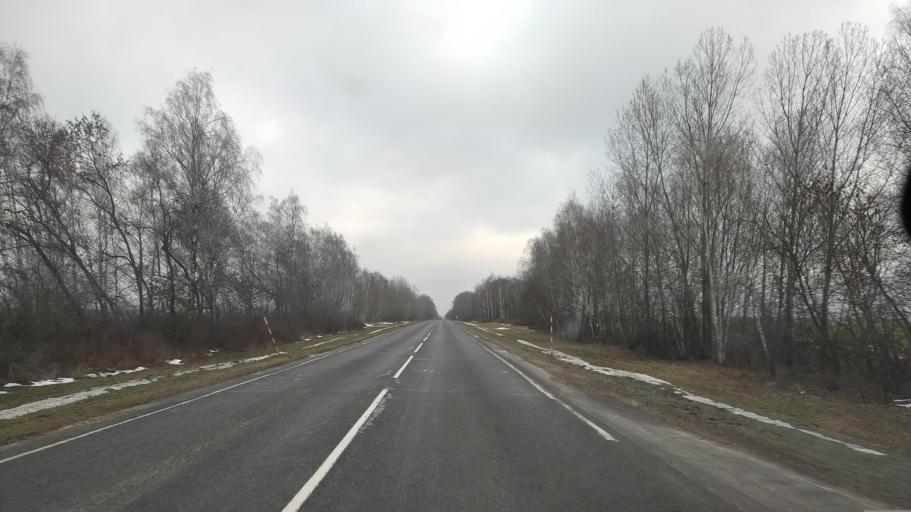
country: BY
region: Brest
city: Byaroza
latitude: 52.5021
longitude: 24.9201
